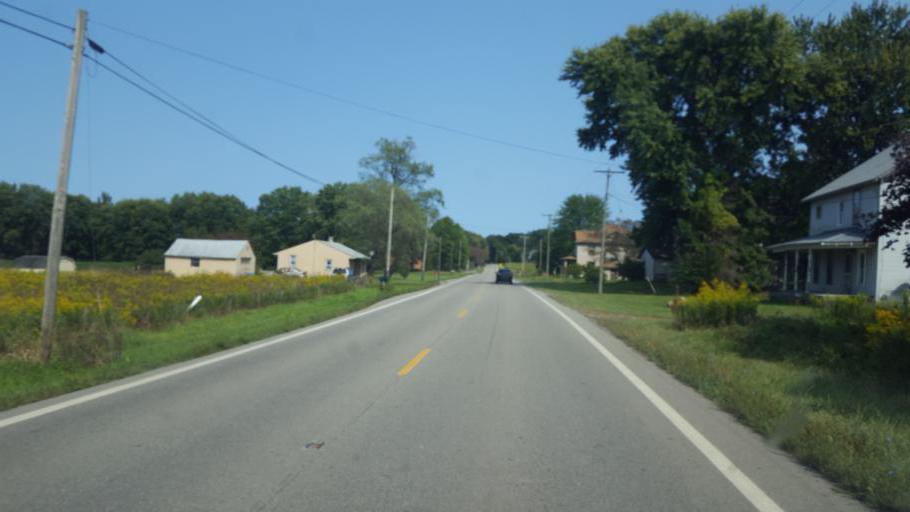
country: US
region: Ohio
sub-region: Wayne County
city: Shreve
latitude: 40.7162
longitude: -82.0705
